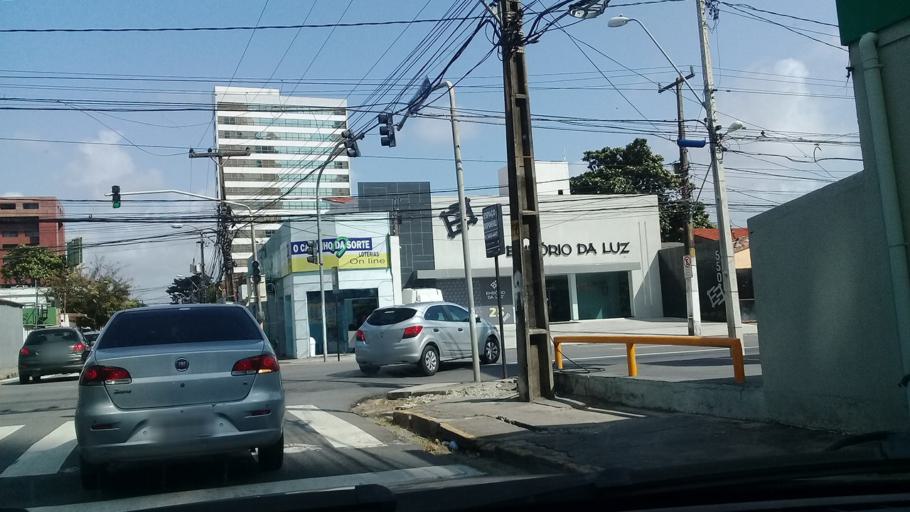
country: BR
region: Pernambuco
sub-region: Recife
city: Recife
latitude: -8.0956
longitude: -34.8844
